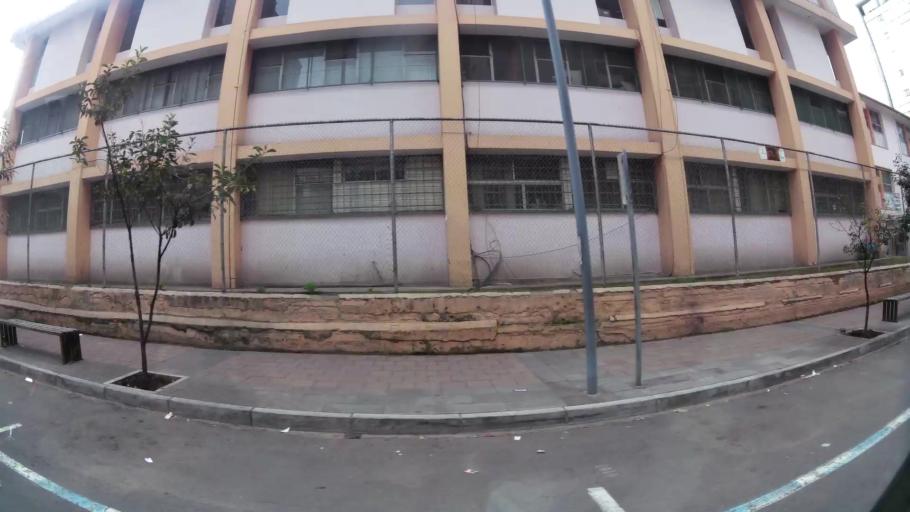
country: EC
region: Pichincha
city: Quito
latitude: -0.1833
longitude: -78.4805
